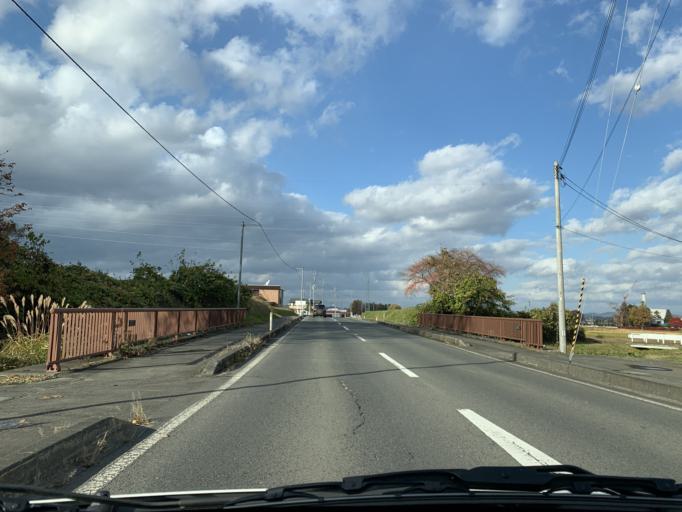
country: JP
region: Iwate
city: Mizusawa
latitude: 39.1537
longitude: 141.1537
